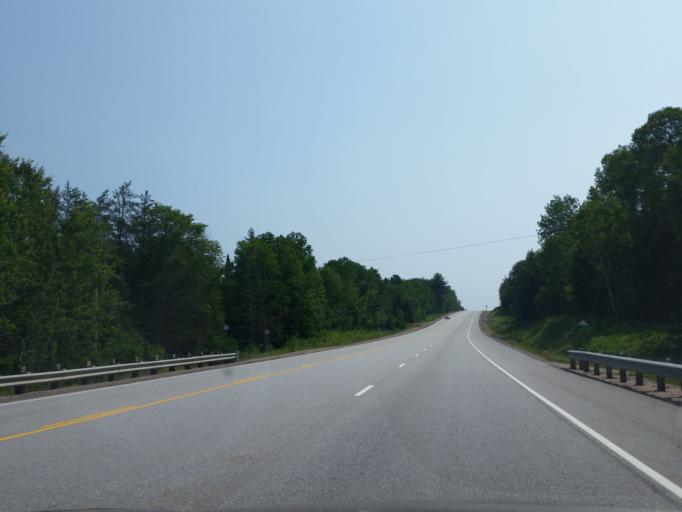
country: CA
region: Ontario
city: Mattawa
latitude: 46.2806
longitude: -78.4291
